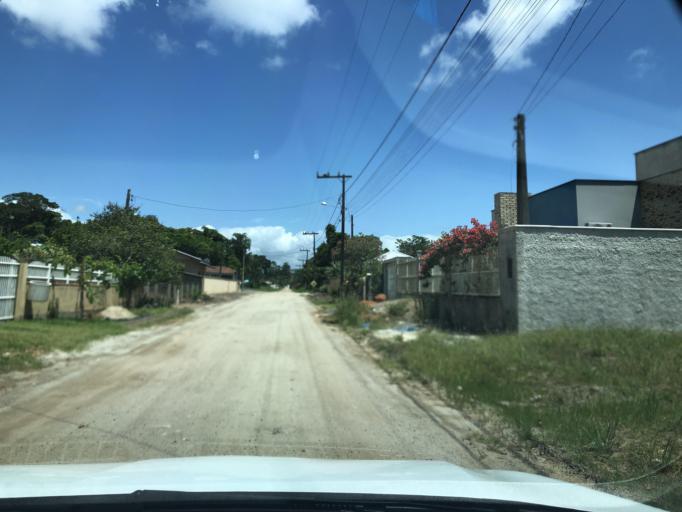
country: BR
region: Santa Catarina
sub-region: Sao Francisco Do Sul
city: Sao Francisco do Sul
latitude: -26.2117
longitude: -48.5326
